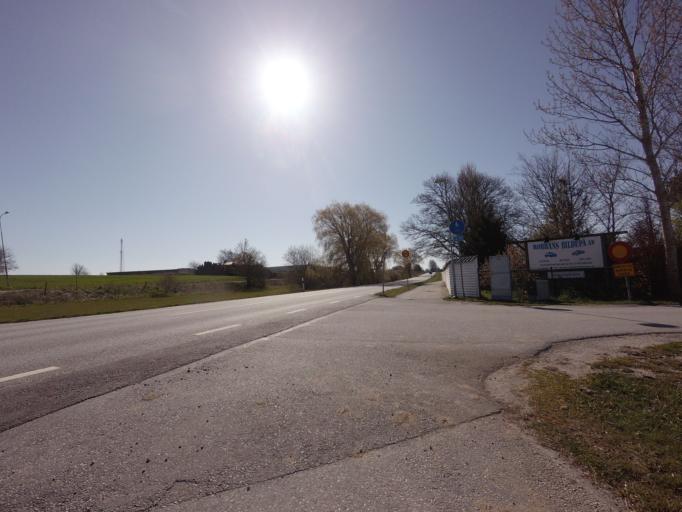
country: SE
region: Skane
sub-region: Malmo
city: Oxie
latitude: 55.4805
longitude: 13.1278
